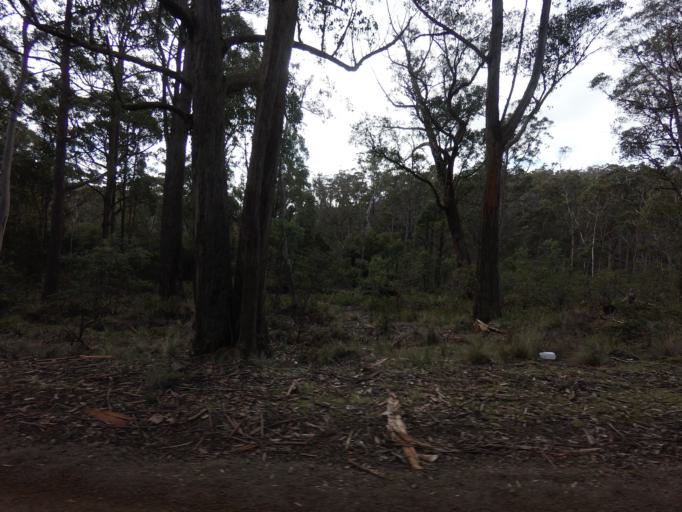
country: AU
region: Tasmania
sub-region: Derwent Valley
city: New Norfolk
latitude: -42.7472
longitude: 146.8671
